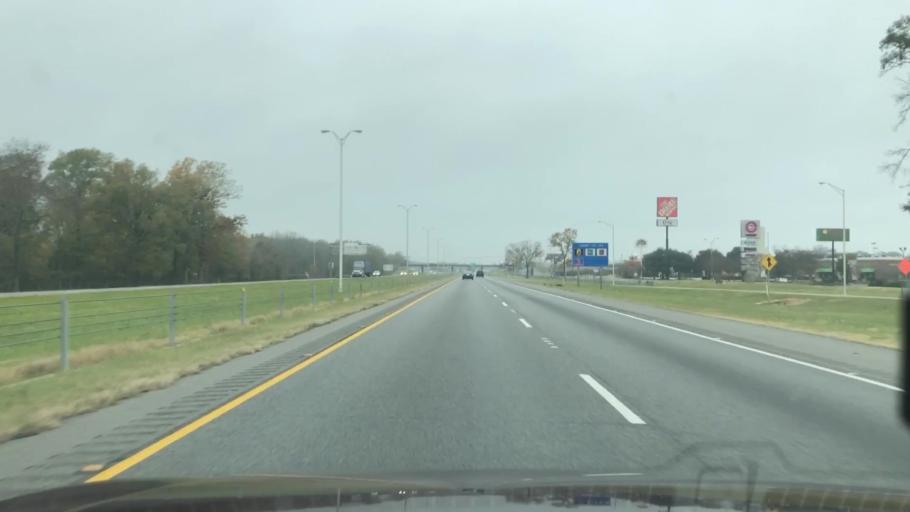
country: US
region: Louisiana
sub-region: Ouachita Parish
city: Richwood
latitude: 32.4973
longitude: -92.0692
